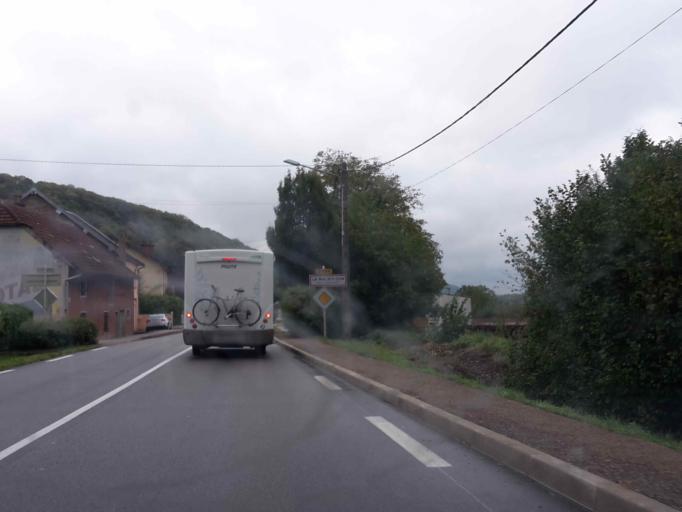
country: FR
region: Franche-Comte
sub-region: Departement du Doubs
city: Novillars
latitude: 47.3001
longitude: 6.1628
